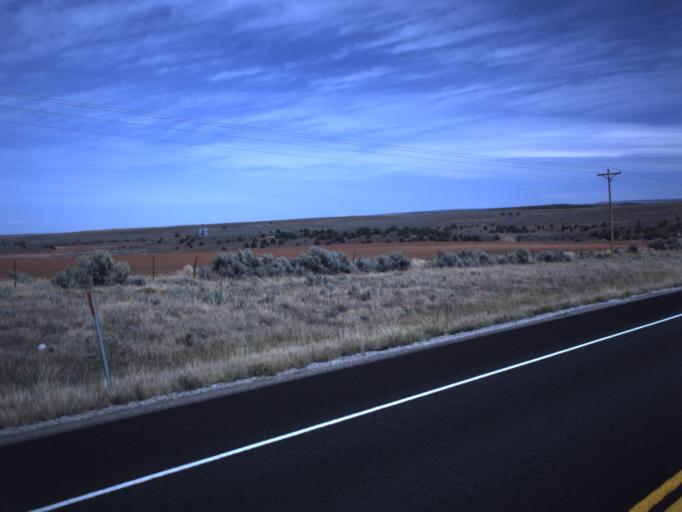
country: US
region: Utah
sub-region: San Juan County
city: Monticello
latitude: 37.8728
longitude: -109.2885
